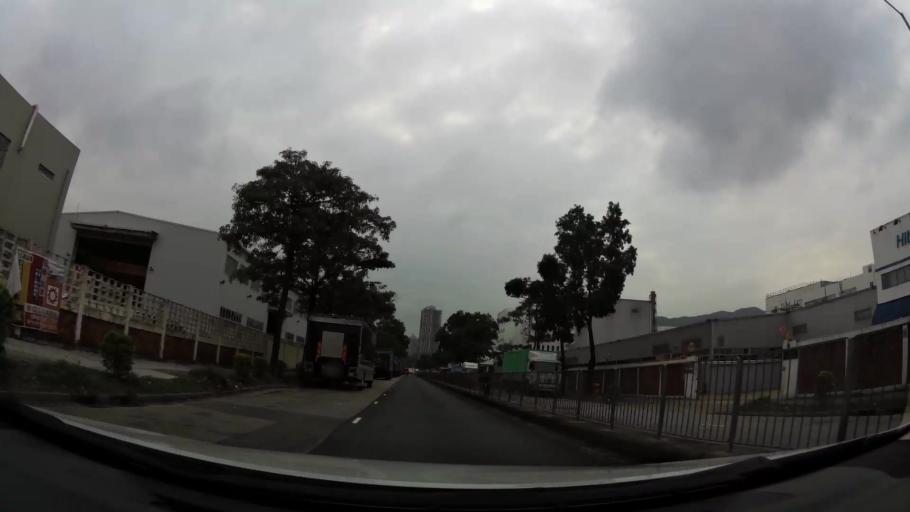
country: HK
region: Tai Po
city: Tai Po
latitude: 22.4570
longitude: 114.1833
